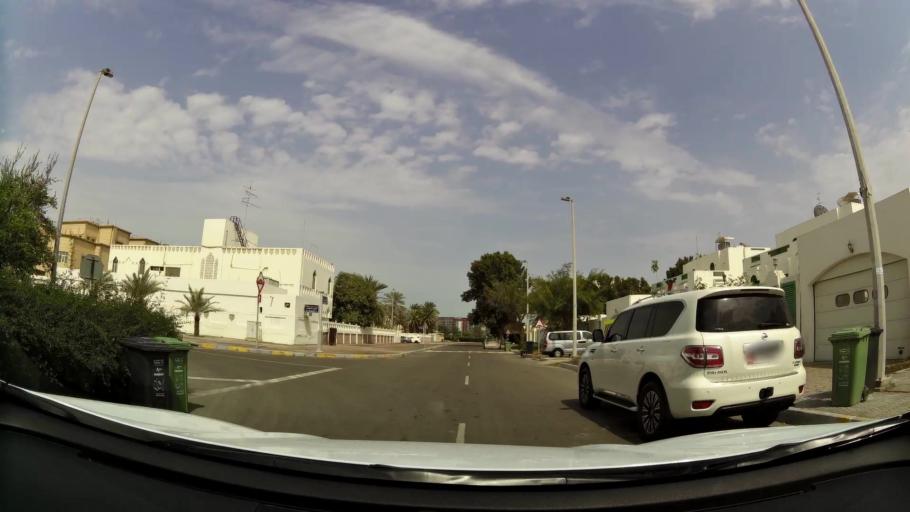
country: AE
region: Abu Dhabi
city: Abu Dhabi
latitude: 24.4141
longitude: 54.4710
